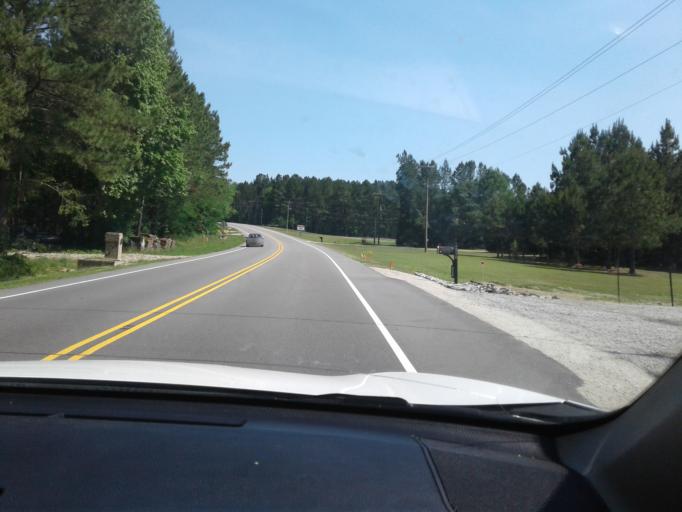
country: US
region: North Carolina
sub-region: Harnett County
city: Lillington
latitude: 35.4401
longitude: -78.8279
